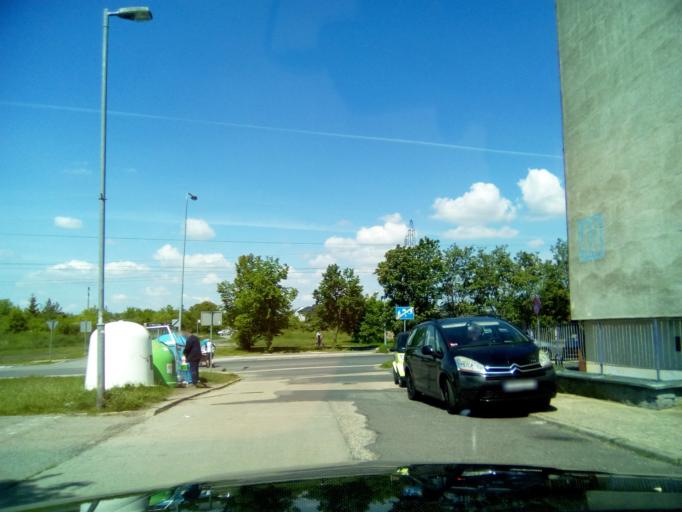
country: PL
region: Greater Poland Voivodeship
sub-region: Powiat gnieznienski
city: Gniezno
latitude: 52.5515
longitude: 17.5982
